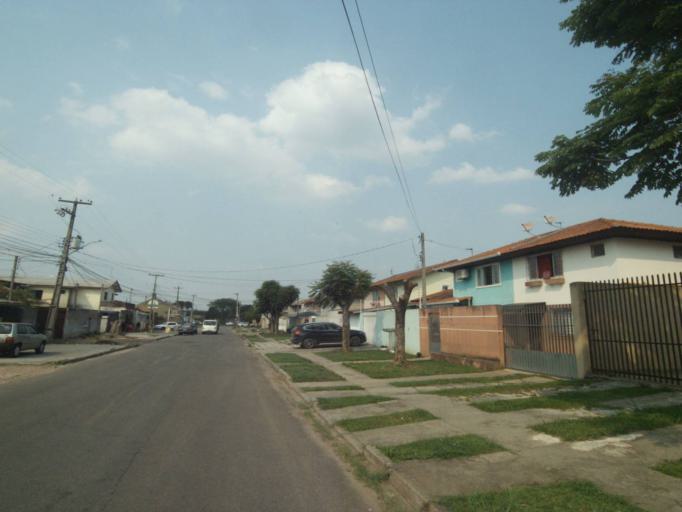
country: BR
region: Parana
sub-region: Sao Jose Dos Pinhais
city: Sao Jose dos Pinhais
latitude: -25.5264
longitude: -49.2291
